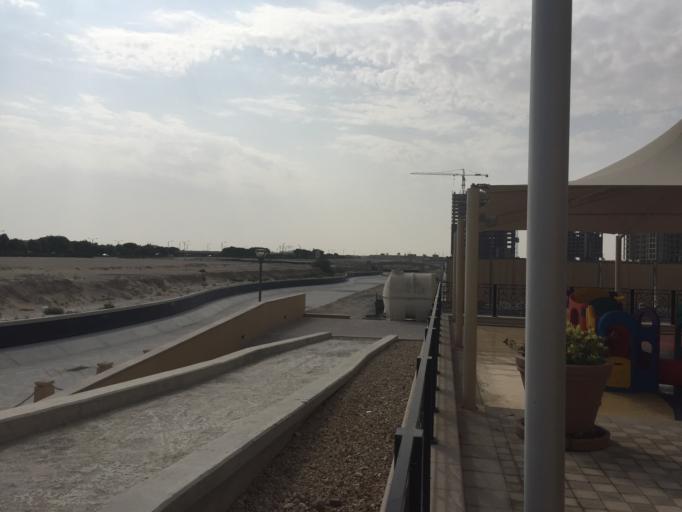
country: AE
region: Dubai
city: Dubai
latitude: 25.0370
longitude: 55.2227
